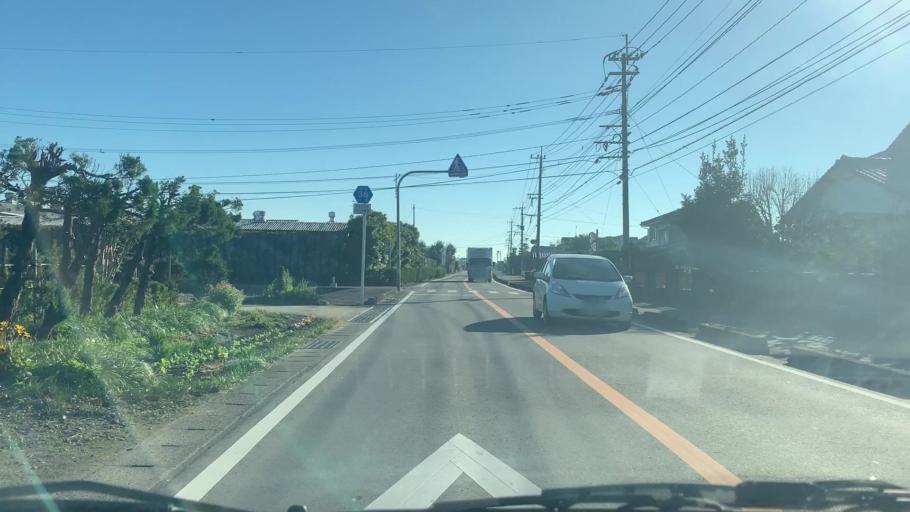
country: JP
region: Saga Prefecture
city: Kashima
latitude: 33.1944
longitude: 130.1151
